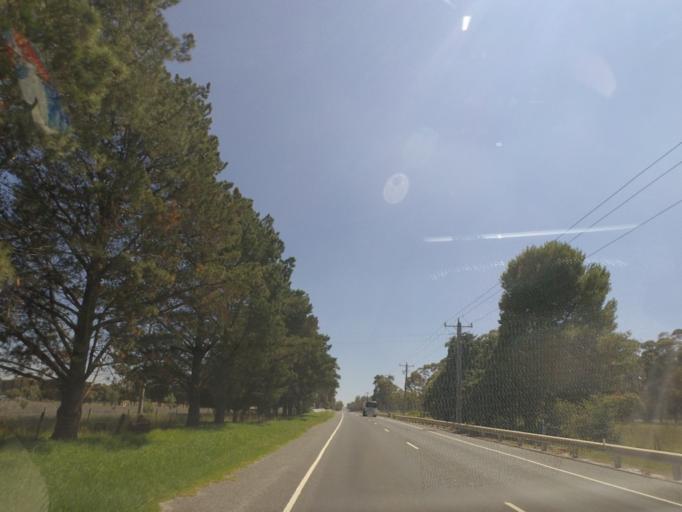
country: AU
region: Victoria
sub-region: Hume
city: Greenvale
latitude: -37.6157
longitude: 144.8391
